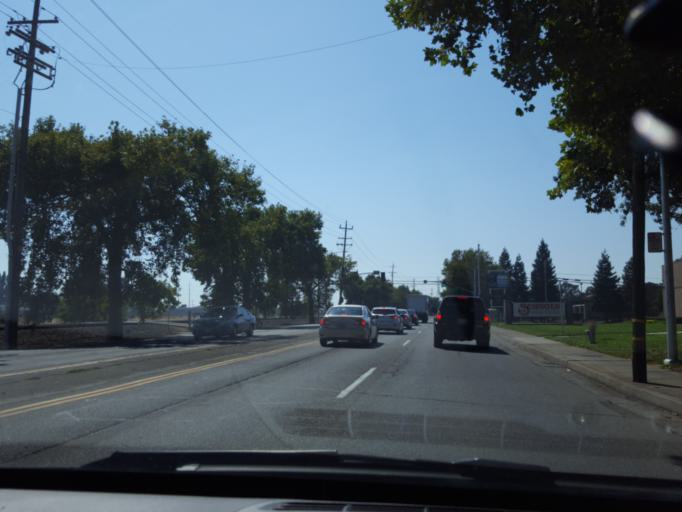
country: US
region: California
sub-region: Sacramento County
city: Rosemont
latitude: 38.5508
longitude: -121.3800
